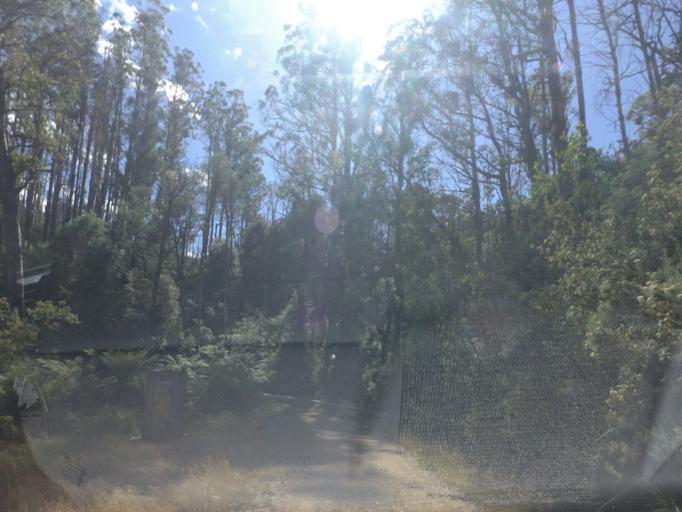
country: AU
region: Victoria
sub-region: Yarra Ranges
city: Millgrove
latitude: -37.4901
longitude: 145.8413
